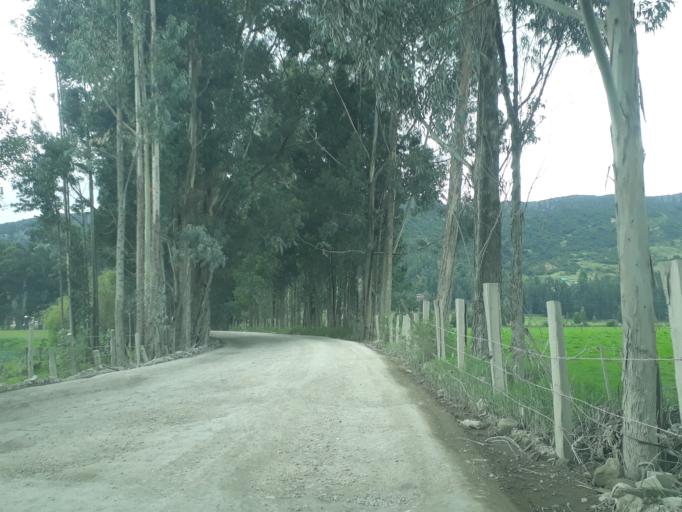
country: CO
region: Cundinamarca
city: Lenguazaque
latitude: 5.3316
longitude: -73.7093
